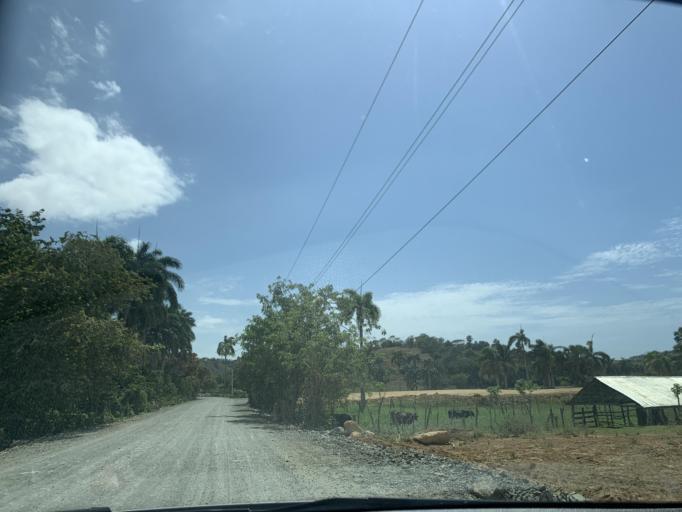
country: DO
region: Puerto Plata
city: Luperon
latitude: 19.8827
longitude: -70.8472
